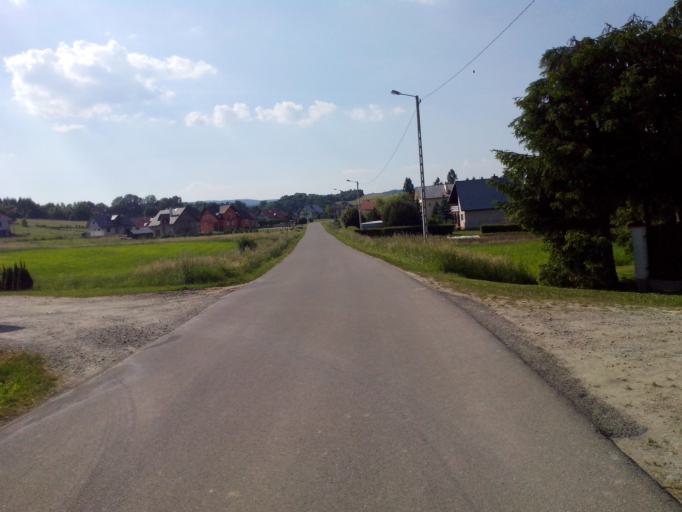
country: PL
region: Subcarpathian Voivodeship
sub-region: Powiat brzozowski
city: Blizne
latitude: 49.7549
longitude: 21.9611
